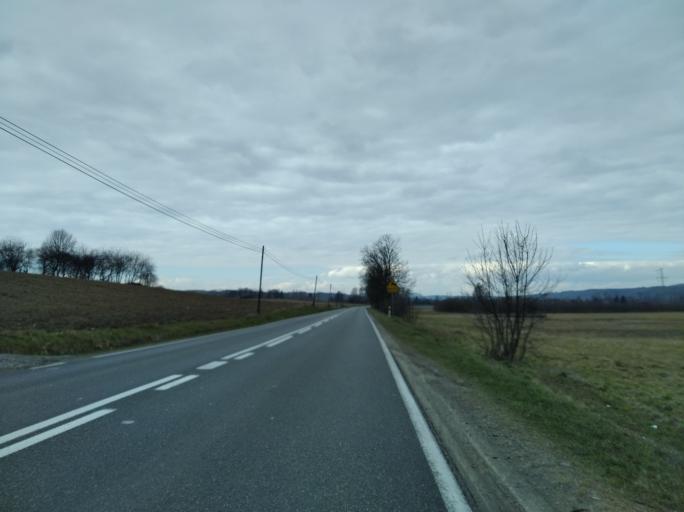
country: PL
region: Subcarpathian Voivodeship
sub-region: Powiat krosnienski
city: Wojaszowka
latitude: 49.7854
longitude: 21.6630
